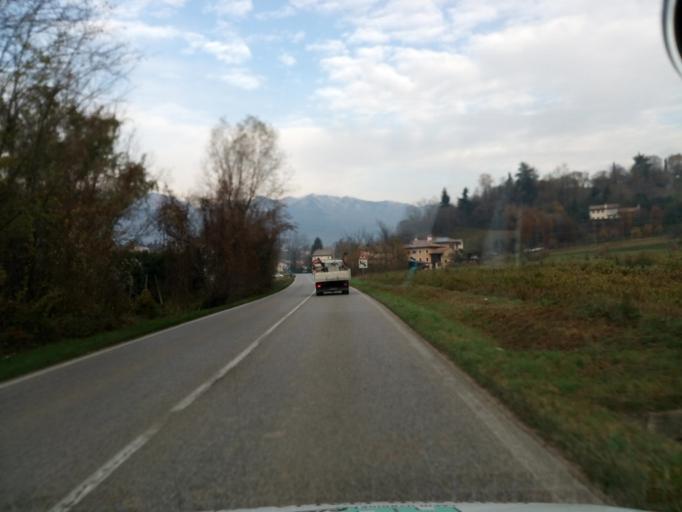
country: IT
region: Veneto
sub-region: Provincia di Treviso
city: Asolo
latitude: 45.8016
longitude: 11.8961
